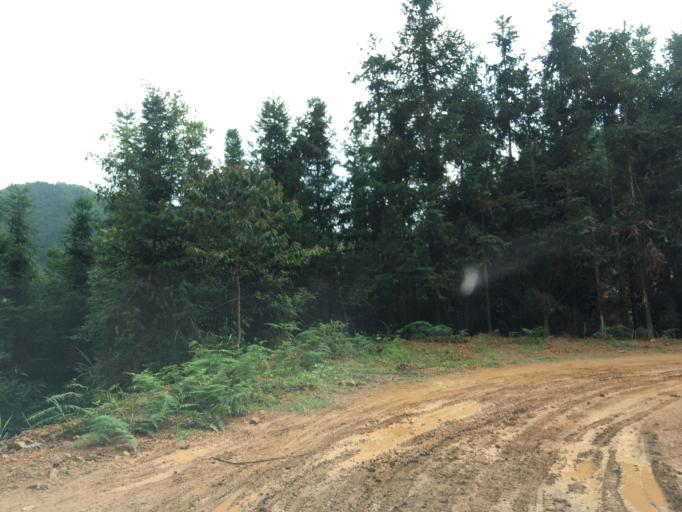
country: CN
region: Guangxi Zhuangzu Zizhiqu
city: Xinzhou
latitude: 24.8678
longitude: 105.8486
